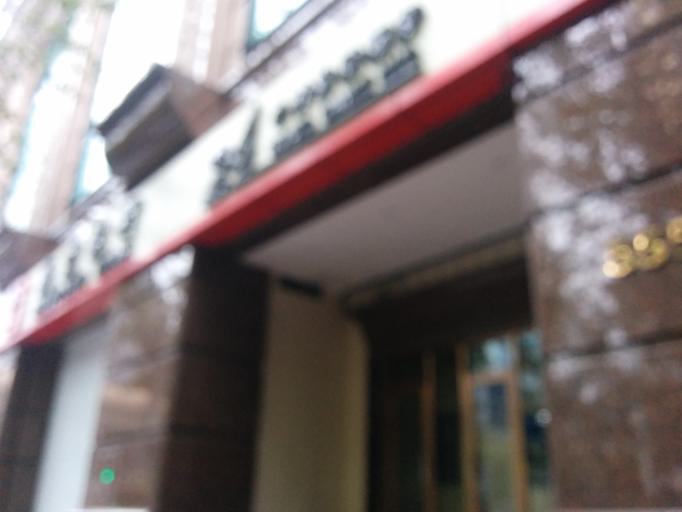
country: CN
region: Shanghai Shi
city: Shanghai
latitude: 31.2329
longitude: 121.4616
